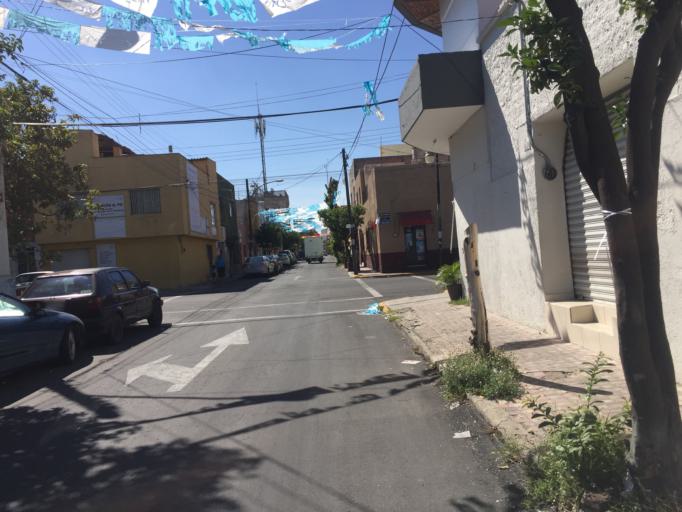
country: MX
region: Jalisco
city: Guadalajara
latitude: 20.6870
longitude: -103.3667
